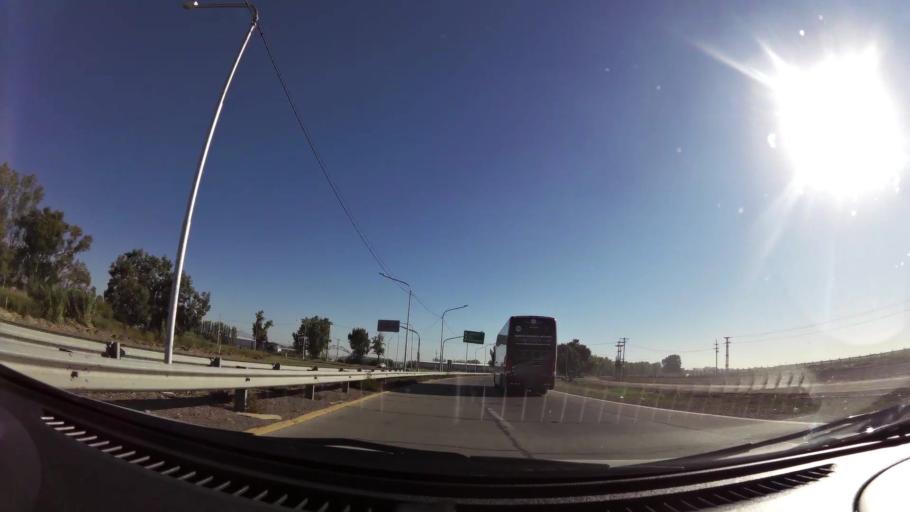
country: AR
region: Mendoza
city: Las Heras
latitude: -32.8227
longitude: -68.8029
